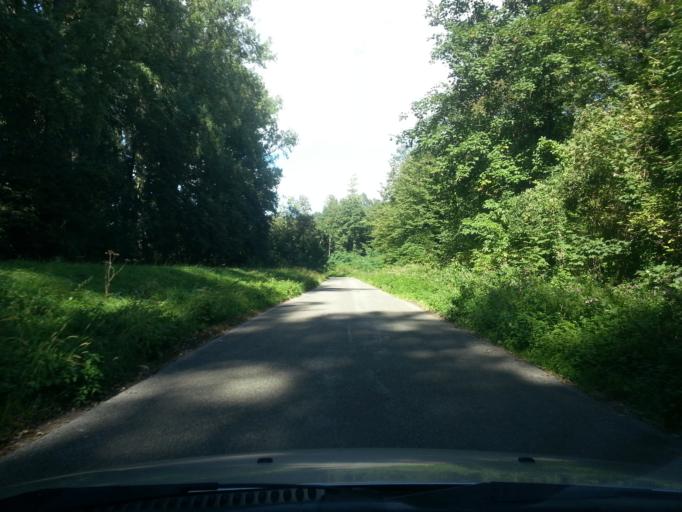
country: DE
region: Rheinland-Pfalz
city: Germersheim
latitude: 49.2185
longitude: 8.3919
